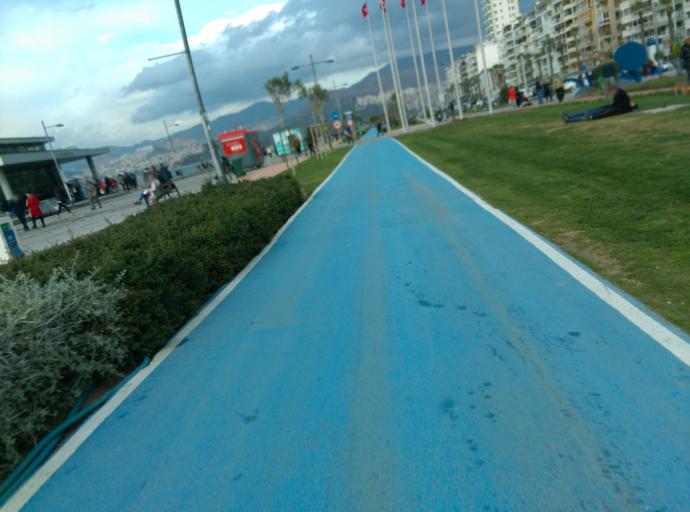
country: TR
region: Izmir
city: Izmir
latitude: 38.4384
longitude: 27.1411
